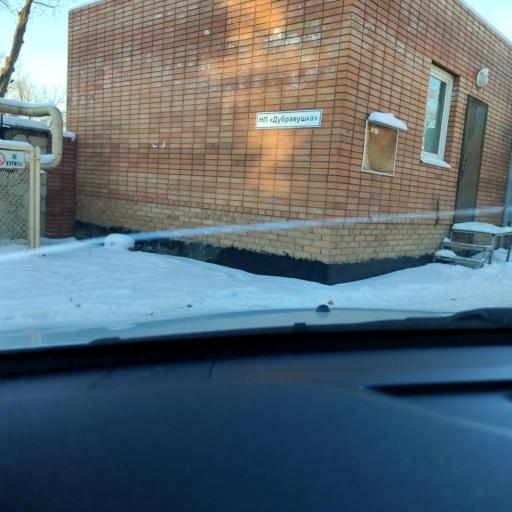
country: RU
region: Samara
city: Samara
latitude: 53.2625
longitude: 50.1888
